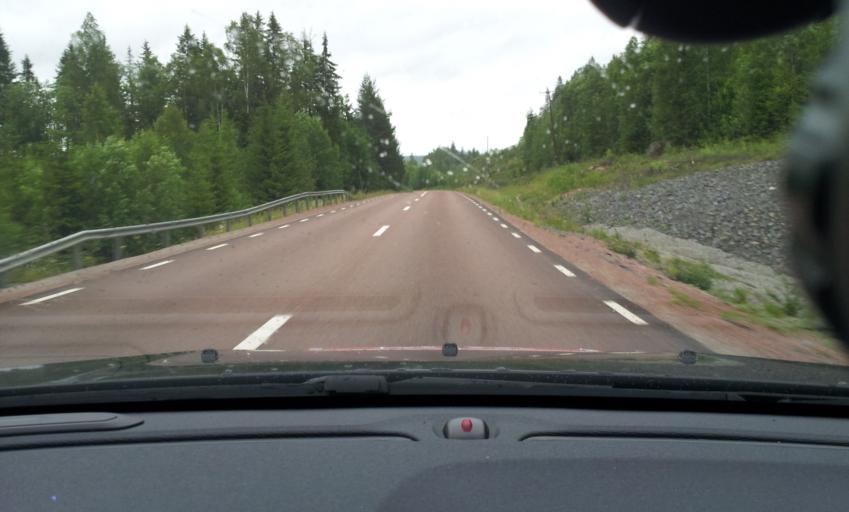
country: SE
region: Jaemtland
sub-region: Ragunda Kommun
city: Hammarstrand
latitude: 63.0600
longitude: 16.4488
